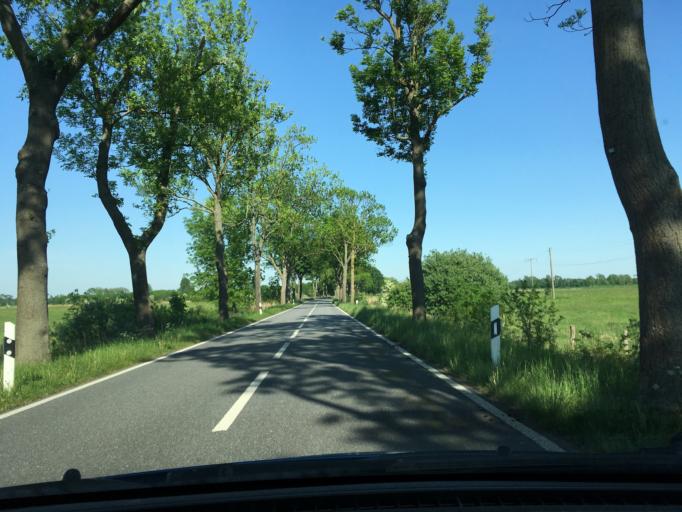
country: DE
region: Brandenburg
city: Lenzen
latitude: 53.0847
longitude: 11.4489
